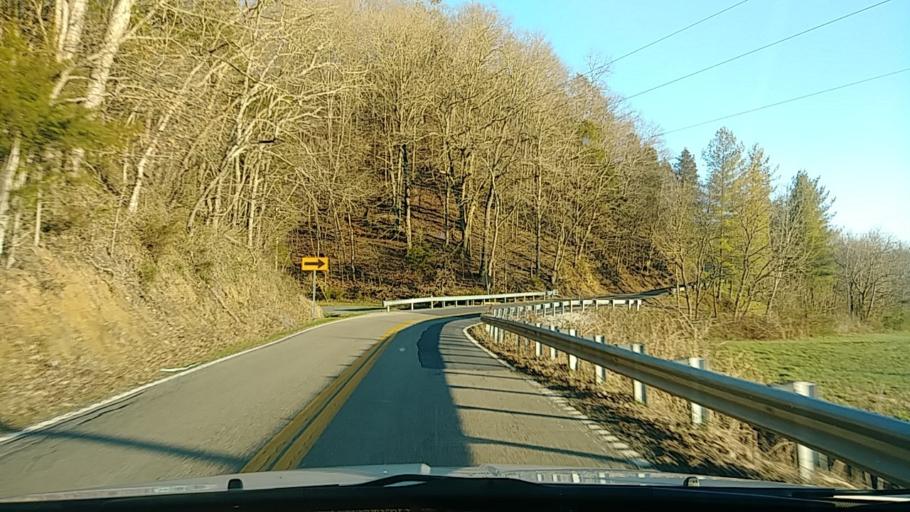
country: US
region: Tennessee
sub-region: Jefferson County
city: White Pine
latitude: 36.1264
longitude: -83.1241
